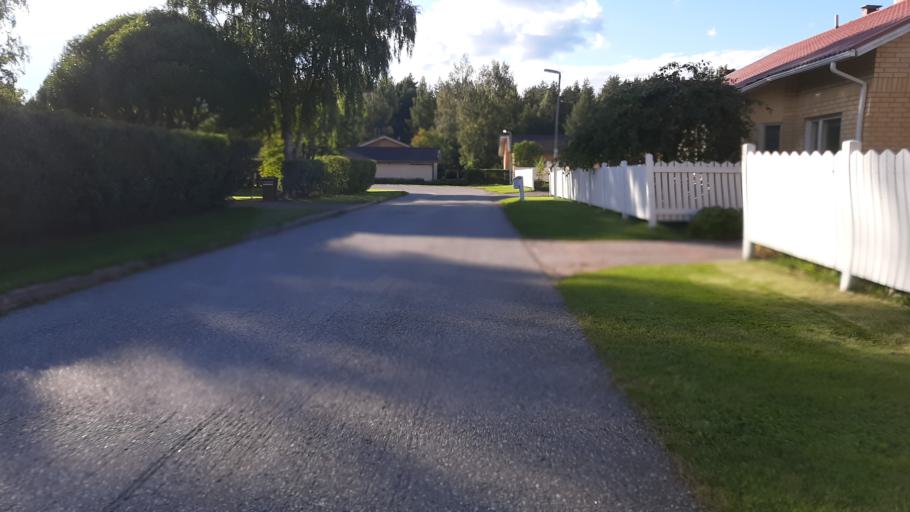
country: FI
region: North Karelia
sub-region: Joensuu
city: Joensuu
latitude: 62.6249
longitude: 29.7974
